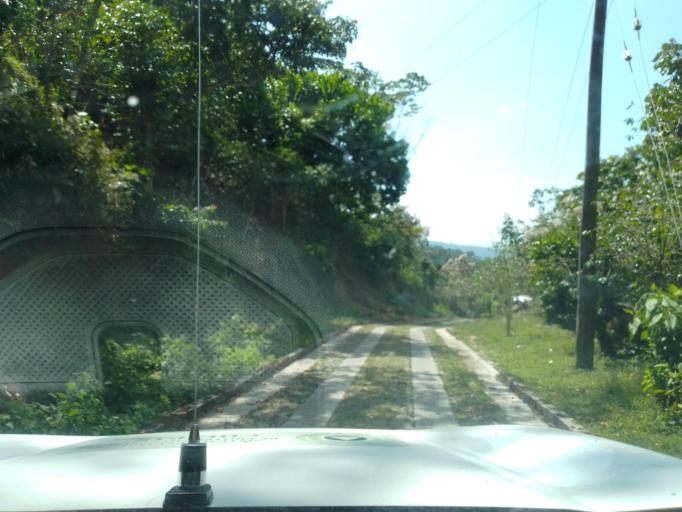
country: MX
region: Chiapas
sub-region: Union Juarez
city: Santo Domingo
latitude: 15.0713
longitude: -92.0908
